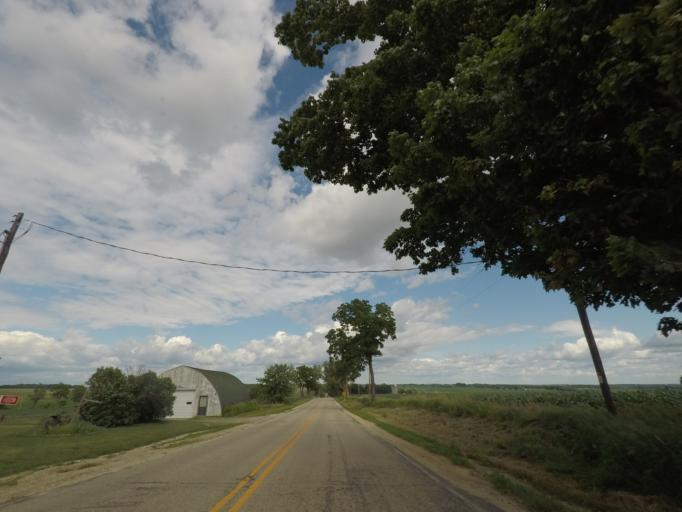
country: US
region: Wisconsin
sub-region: Rock County
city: Orfordville
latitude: 42.7116
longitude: -89.2040
